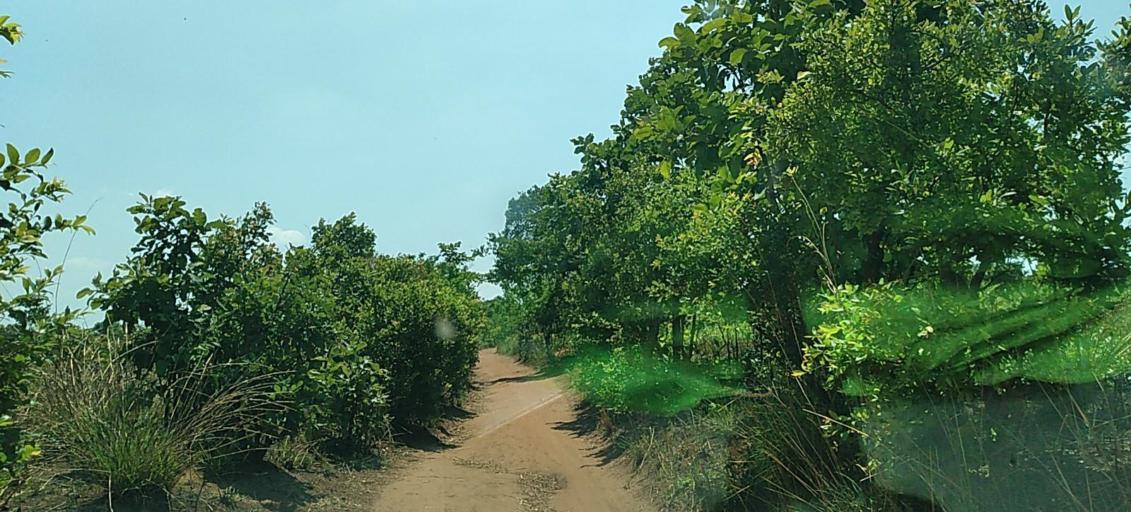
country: CD
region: Katanga
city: Kolwezi
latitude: -11.2904
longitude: 25.2043
